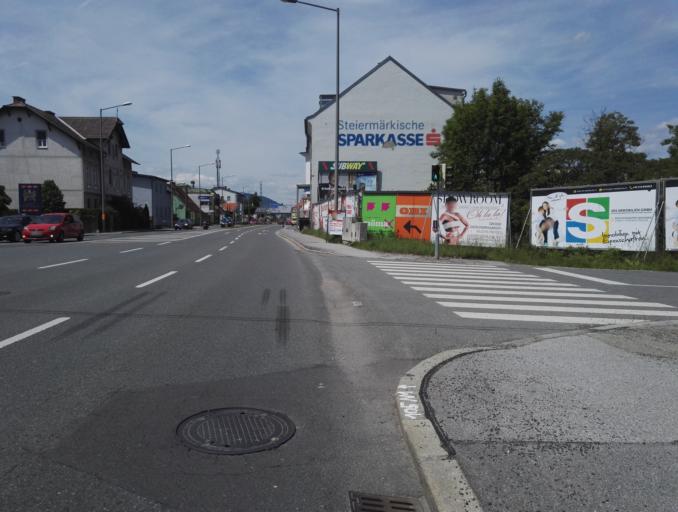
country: AT
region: Styria
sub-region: Politischer Bezirk Graz-Umgebung
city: Feldkirchen bei Graz
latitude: 47.0268
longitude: 15.4343
